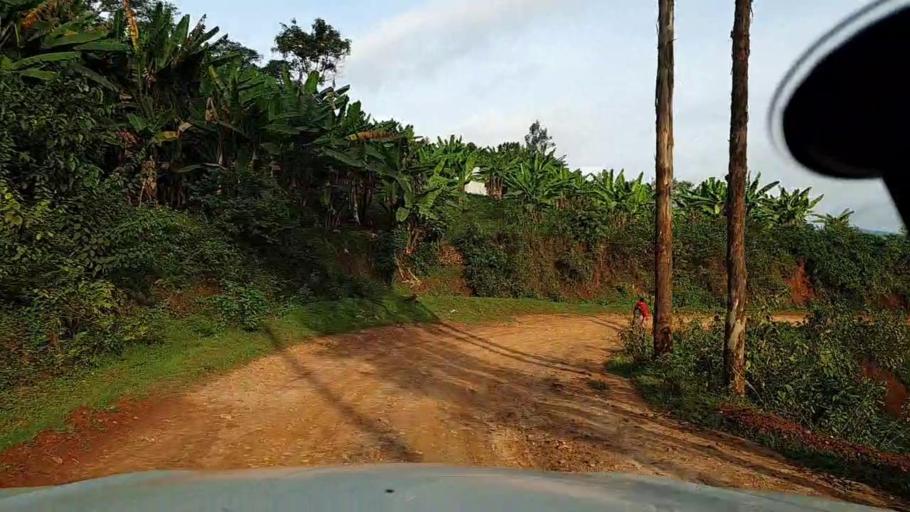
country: RW
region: Southern Province
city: Gitarama
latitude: -2.1878
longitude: 29.5740
